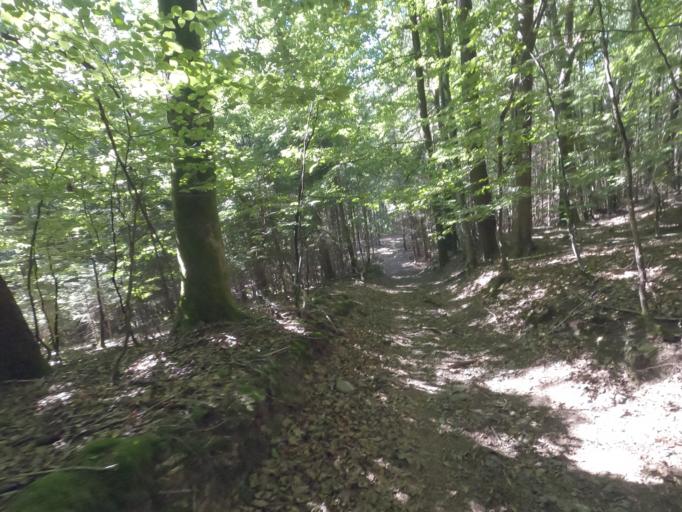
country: DE
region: Bavaria
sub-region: Lower Bavaria
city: Schaufling
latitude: 48.8313
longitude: 13.0194
